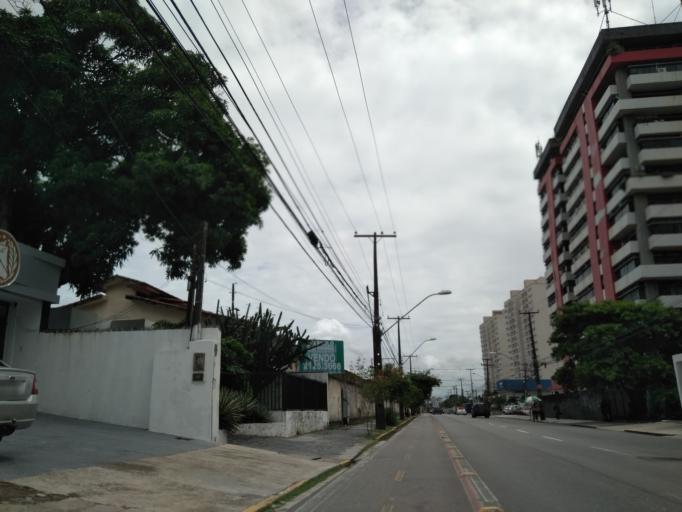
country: BR
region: Pernambuco
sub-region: Recife
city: Recife
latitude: -8.1113
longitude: -34.9045
